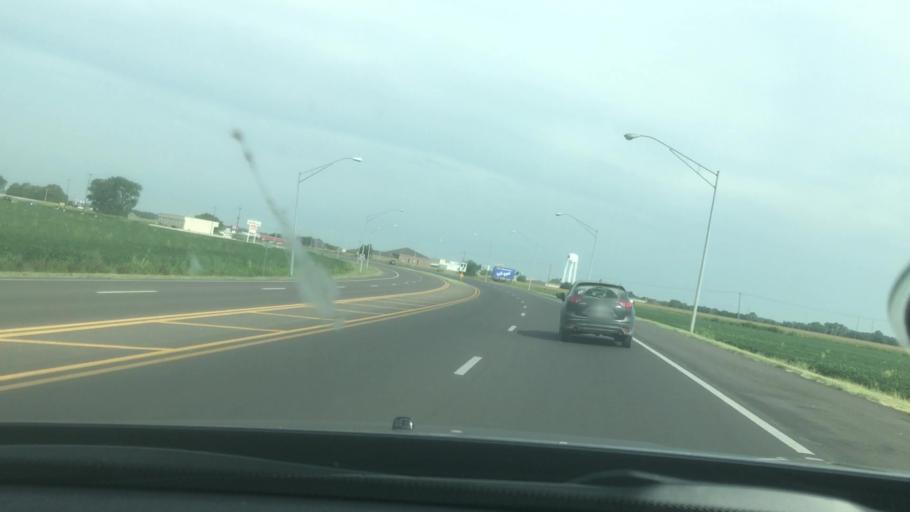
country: US
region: Oklahoma
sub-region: Garvin County
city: Pauls Valley
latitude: 34.7374
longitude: -97.2329
